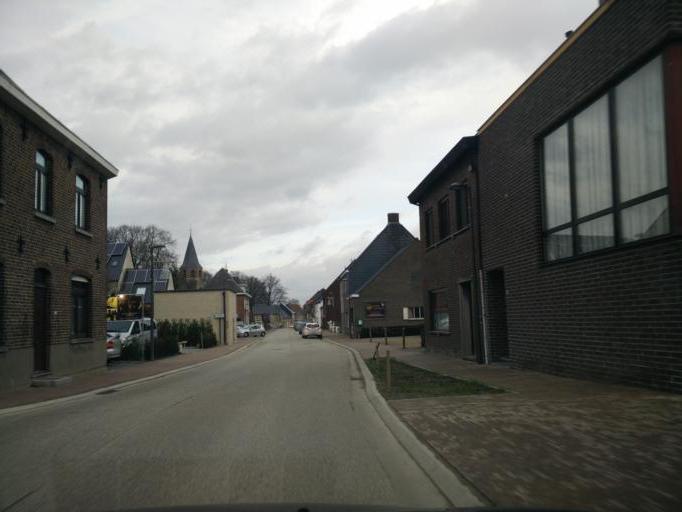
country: BE
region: Flanders
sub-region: Provincie Oost-Vlaanderen
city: Merelbeke
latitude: 50.9702
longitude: 3.7134
